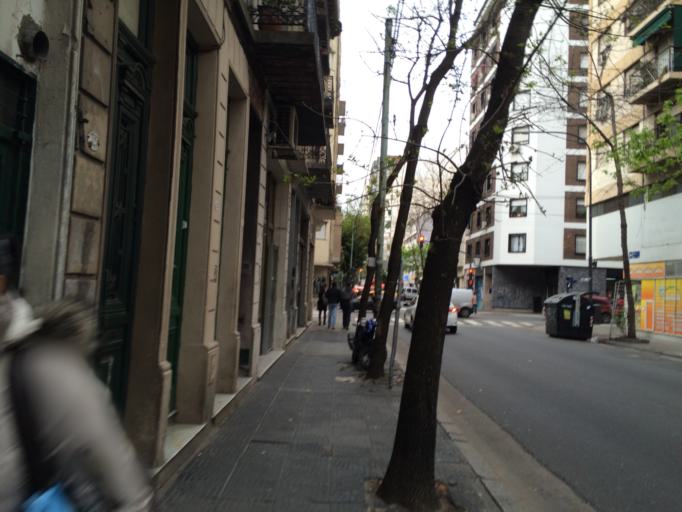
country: AR
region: Buenos Aires F.D.
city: Buenos Aires
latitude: -34.6137
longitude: -58.4014
